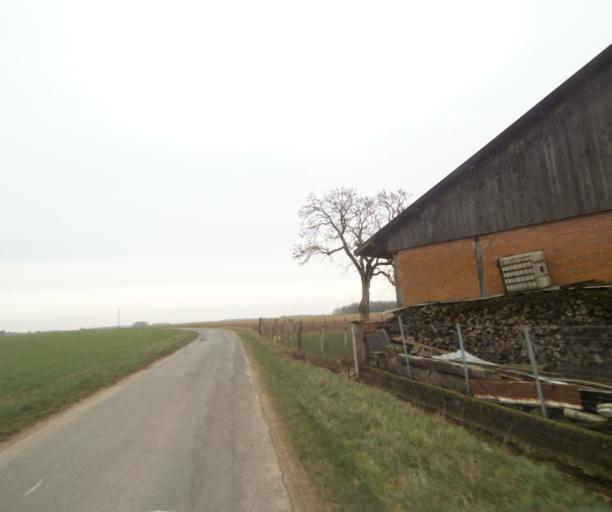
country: FR
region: Champagne-Ardenne
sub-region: Departement de la Haute-Marne
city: Villiers-en-Lieu
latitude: 48.6337
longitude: 4.8143
